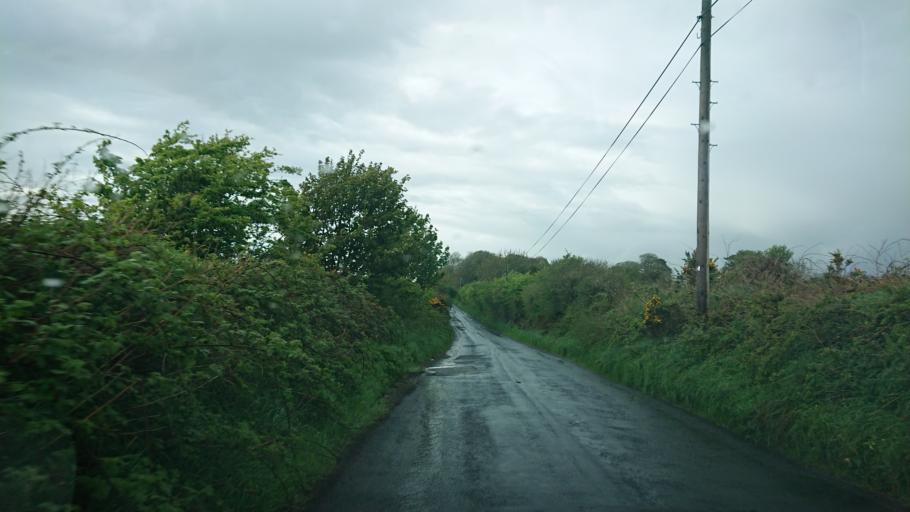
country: IE
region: Munster
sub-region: Waterford
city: Waterford
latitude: 52.2242
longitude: -7.0724
